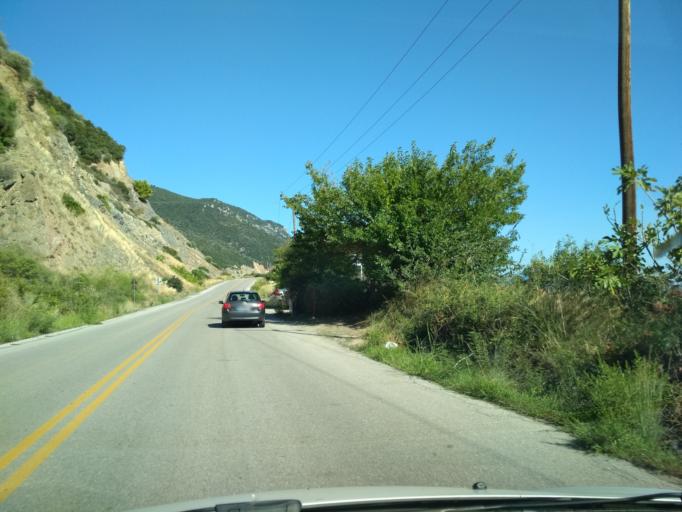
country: GR
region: Central Greece
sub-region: Nomos Evvoias
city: Oreoi
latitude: 38.8528
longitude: 23.1284
